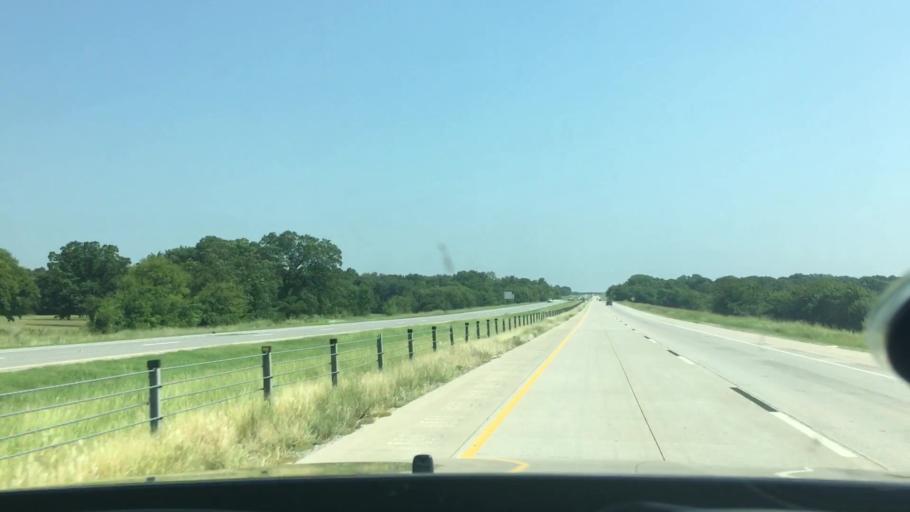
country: US
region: Oklahoma
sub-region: Bryan County
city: Durant
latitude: 34.0583
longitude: -96.3522
